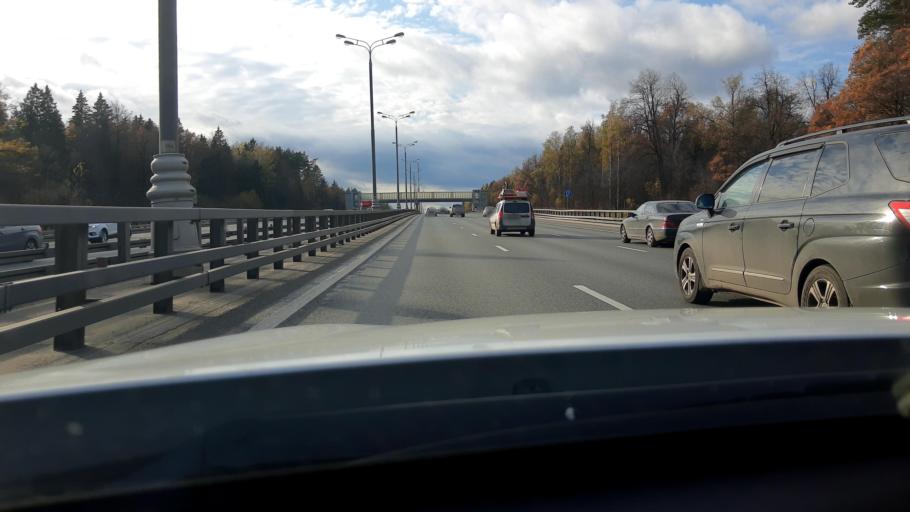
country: RU
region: Moskovskaya
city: Aprelevka
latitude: 55.5443
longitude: 37.1032
